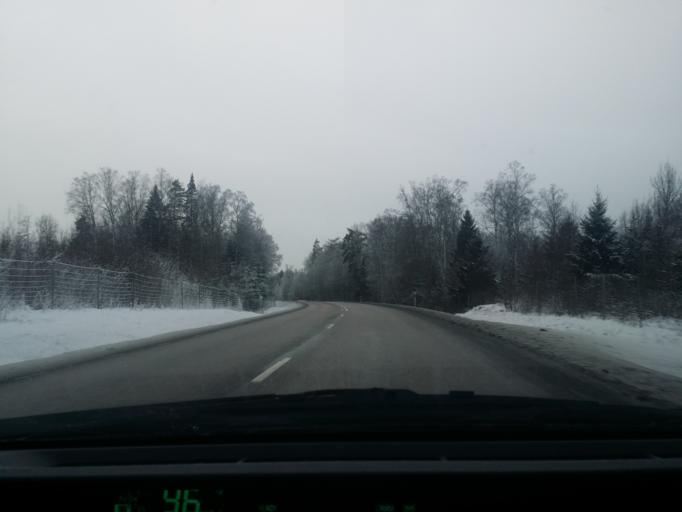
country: SE
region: Vaestra Goetaland
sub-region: Gullspangs Kommun
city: Anderstorp
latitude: 58.8799
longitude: 14.2727
